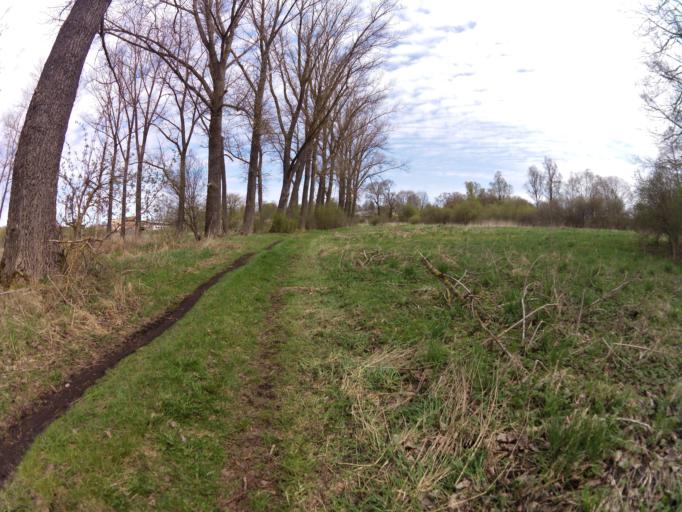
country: PL
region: West Pomeranian Voivodeship
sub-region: Powiat szczecinecki
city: Borne Sulinowo
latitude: 53.7060
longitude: 16.5386
